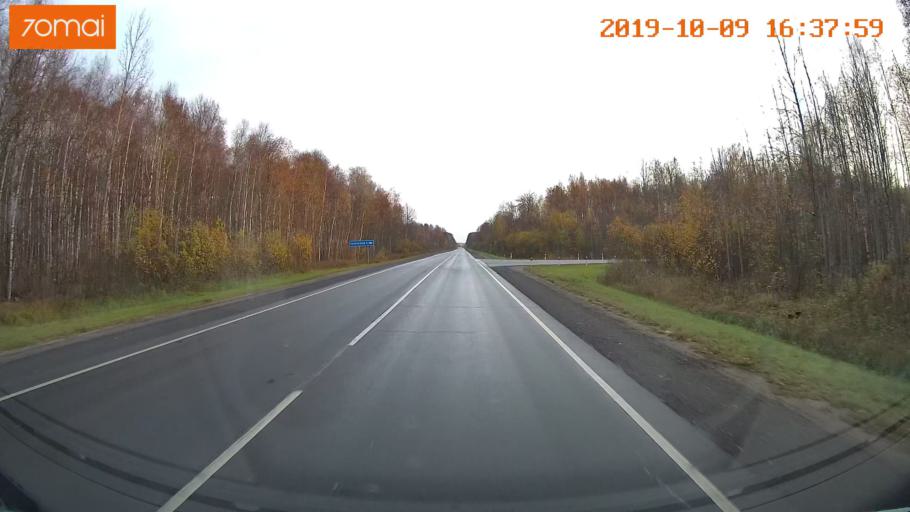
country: RU
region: Kostroma
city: Volgorechensk
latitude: 57.5187
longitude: 41.0315
